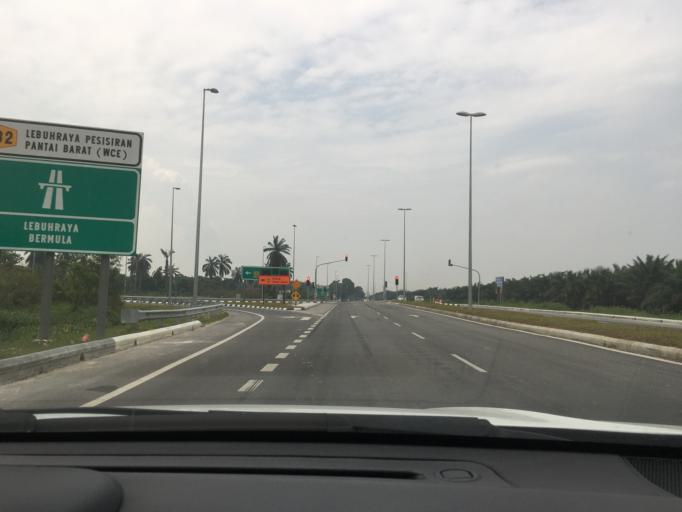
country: MY
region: Perak
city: Kampong Dungun
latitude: 3.1364
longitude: 101.3976
